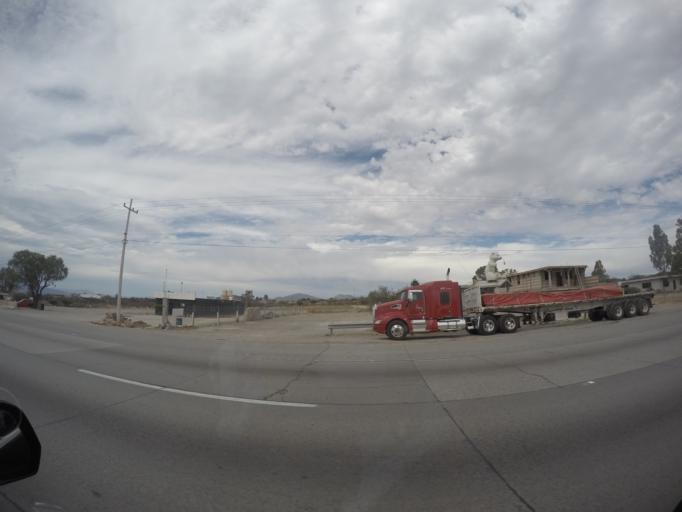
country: MX
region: Queretaro
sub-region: San Juan del Rio
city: Paso de Mata
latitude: 20.3448
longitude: -99.9469
